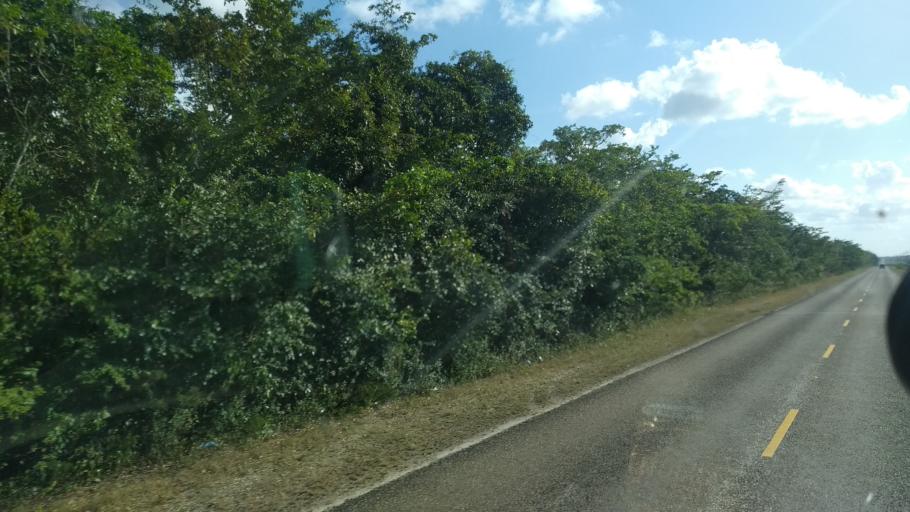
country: BZ
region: Cayo
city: Belmopan
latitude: 17.3800
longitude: -88.5227
